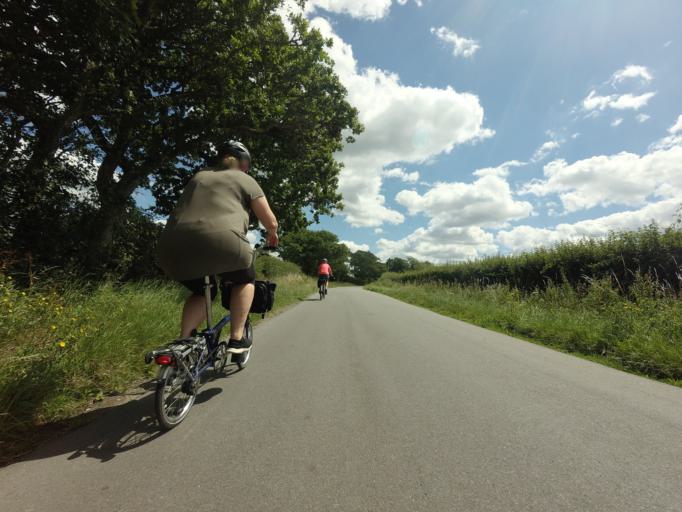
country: GB
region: England
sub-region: East Sussex
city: Seaford
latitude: 50.8562
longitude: 0.1558
